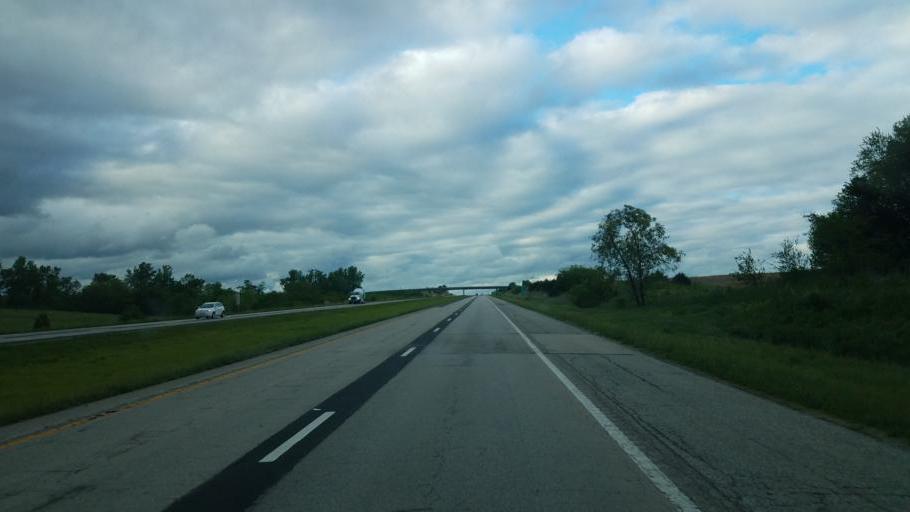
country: US
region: Missouri
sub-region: Harrison County
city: Bethany
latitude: 40.4128
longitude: -93.9919
